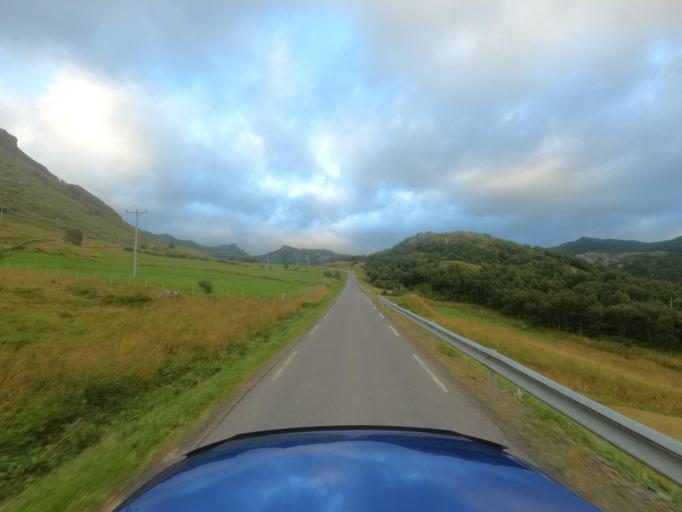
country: NO
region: Nordland
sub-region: Vestvagoy
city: Leknes
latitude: 68.2514
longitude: 13.5874
